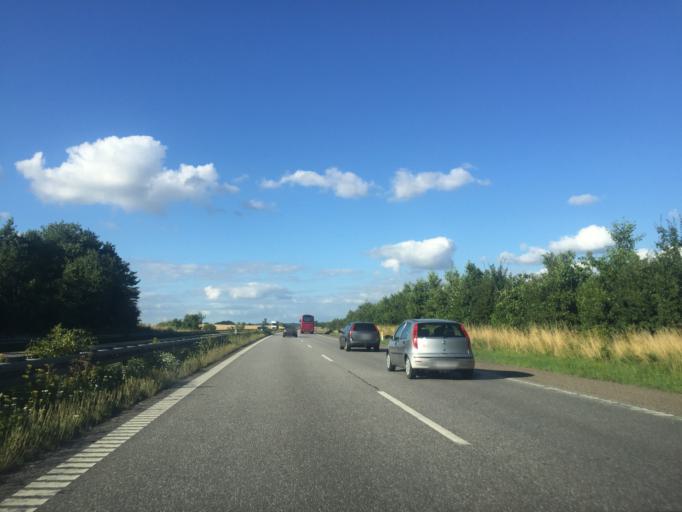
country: DK
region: Zealand
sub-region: Vordingborg Kommune
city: Orslev
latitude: 55.1494
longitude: 11.9440
